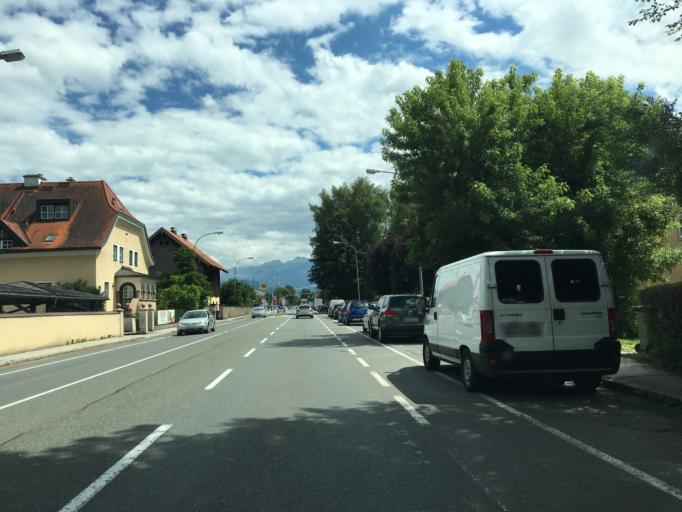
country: AT
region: Salzburg
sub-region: Politischer Bezirk Hallein
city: Hallein
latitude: 47.6810
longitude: 13.1027
